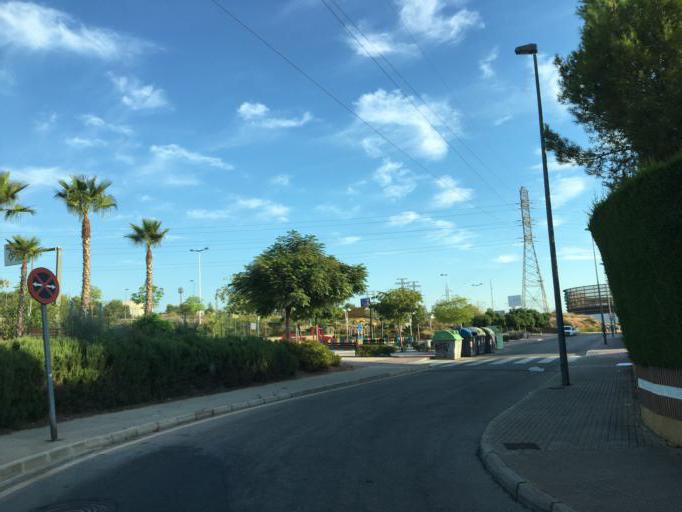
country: ES
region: Murcia
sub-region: Murcia
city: Murcia
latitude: 38.0142
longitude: -1.1655
